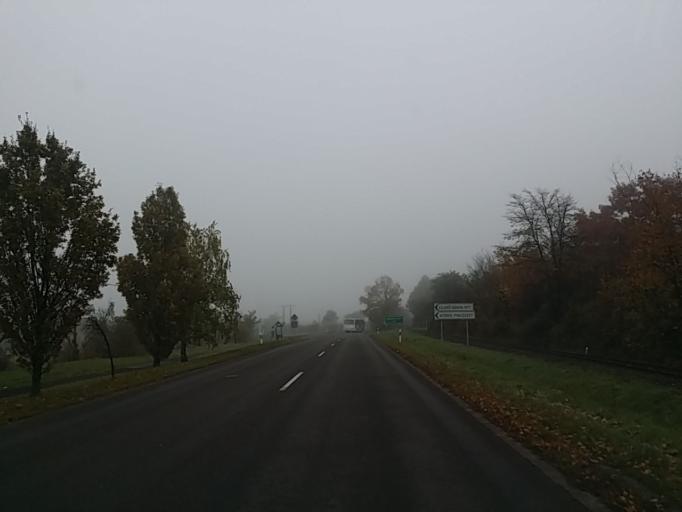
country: HU
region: Heves
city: Gyongyossolymos
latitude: 47.8150
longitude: 19.9588
